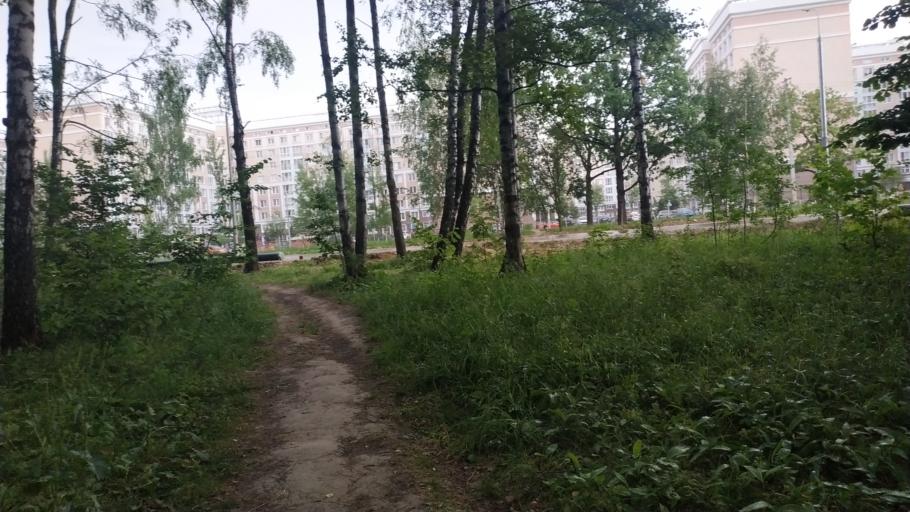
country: RU
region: Moskovskaya
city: Mosrentgen
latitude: 55.5871
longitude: 37.4547
